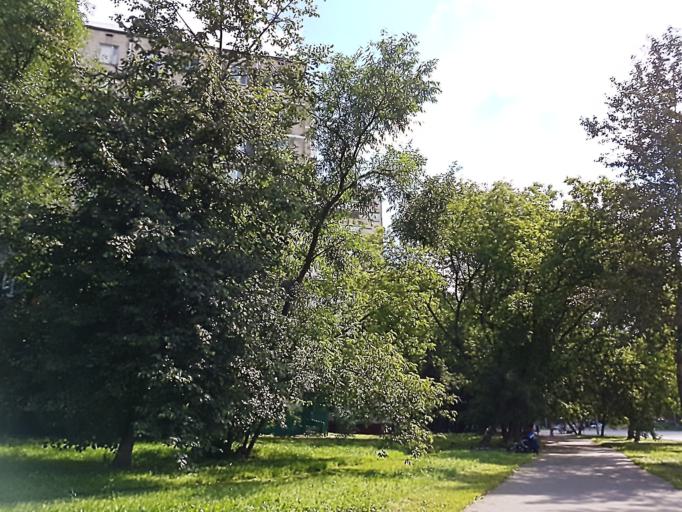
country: RU
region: Moskovskaya
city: Kuskovo
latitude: 55.7389
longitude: 37.8187
